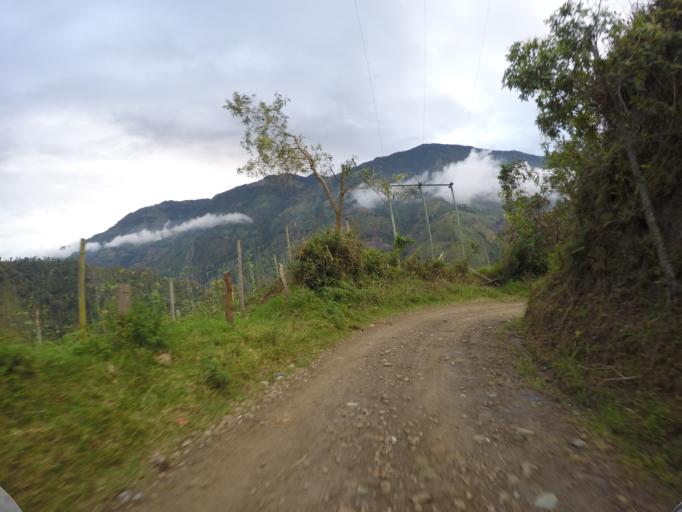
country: CO
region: Tolima
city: Cajamarca
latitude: 4.5055
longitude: -75.4010
